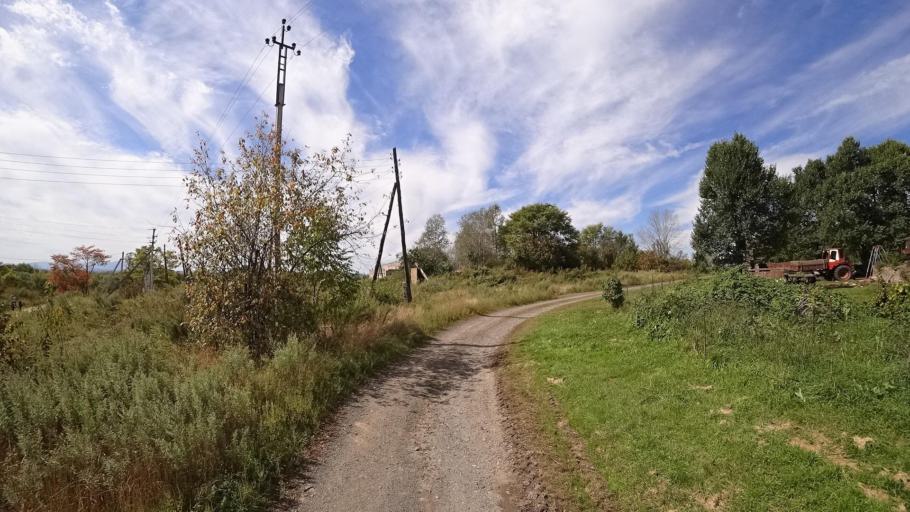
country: RU
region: Primorskiy
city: Yakovlevka
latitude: 44.6410
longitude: 133.5892
